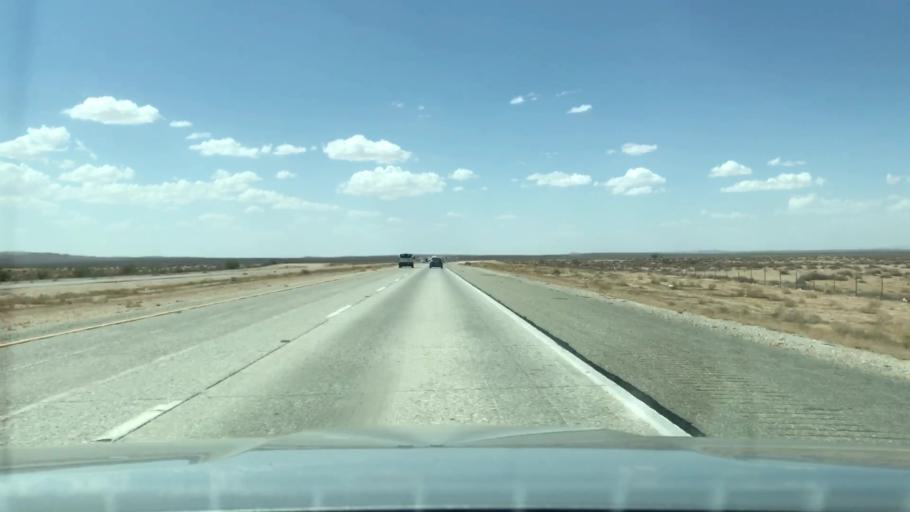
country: US
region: California
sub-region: San Bernardino County
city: Lenwood
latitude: 34.9263
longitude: -117.3460
